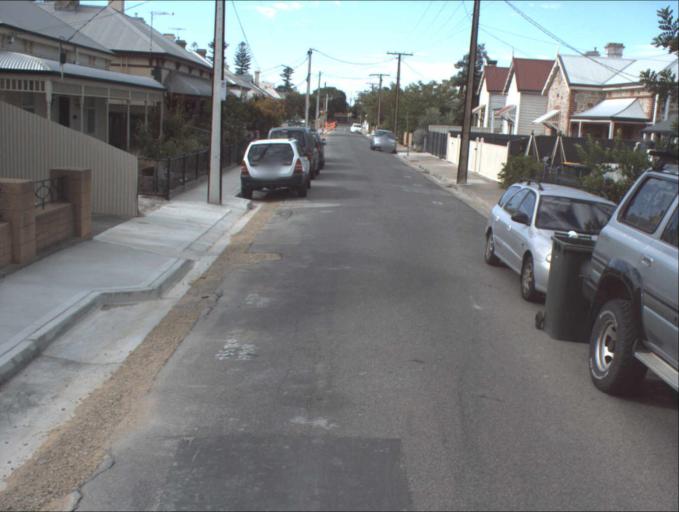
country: AU
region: South Australia
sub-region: Port Adelaide Enfield
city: Birkenhead
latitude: -34.8356
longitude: 138.4839
